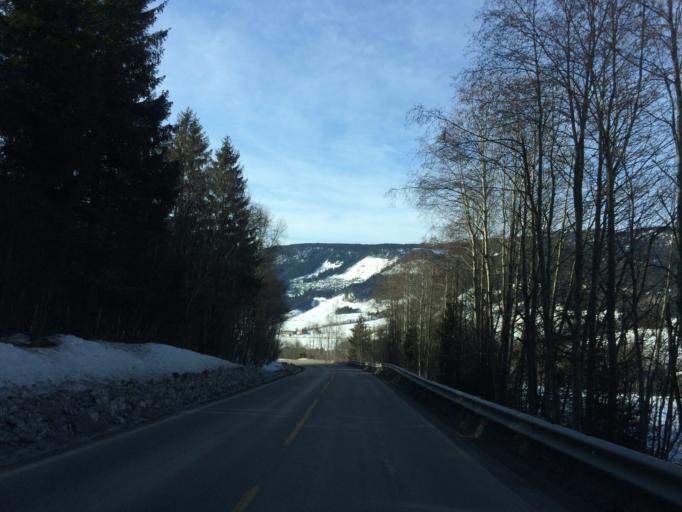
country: NO
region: Oppland
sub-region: Gausdal
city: Segalstad bru
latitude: 61.2762
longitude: 10.1472
